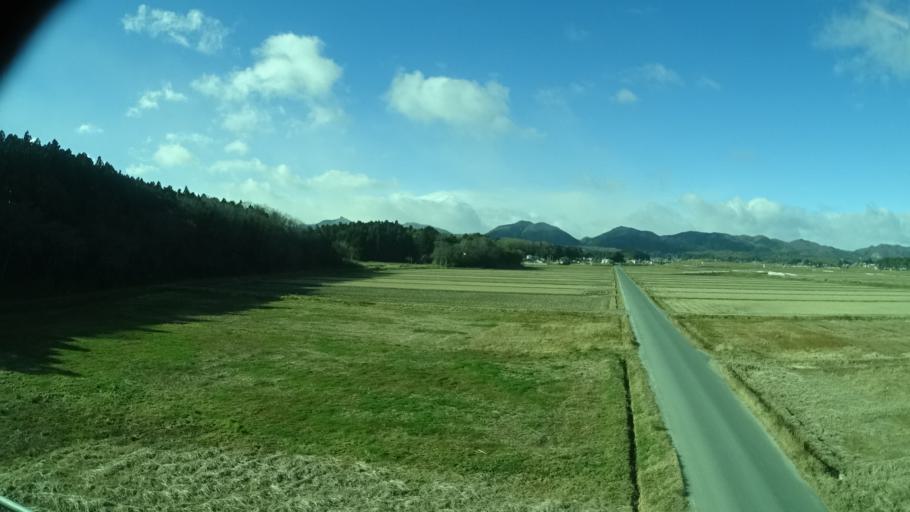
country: JP
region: Miyagi
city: Marumori
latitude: 37.8886
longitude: 140.9222
